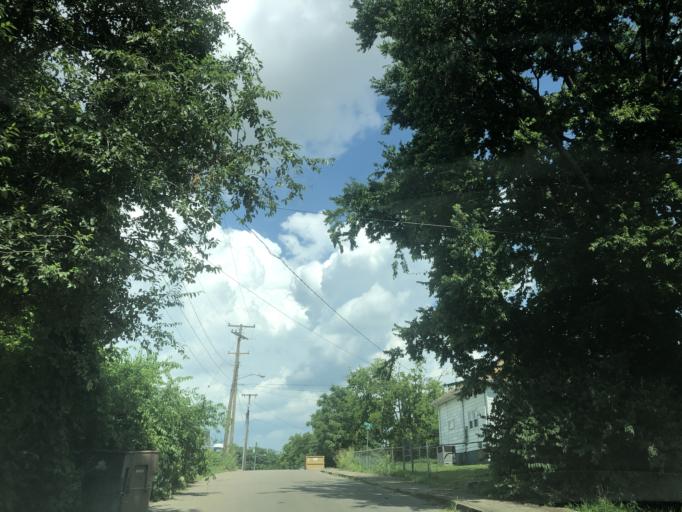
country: US
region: Tennessee
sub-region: Davidson County
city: Nashville
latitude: 36.1611
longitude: -86.8117
